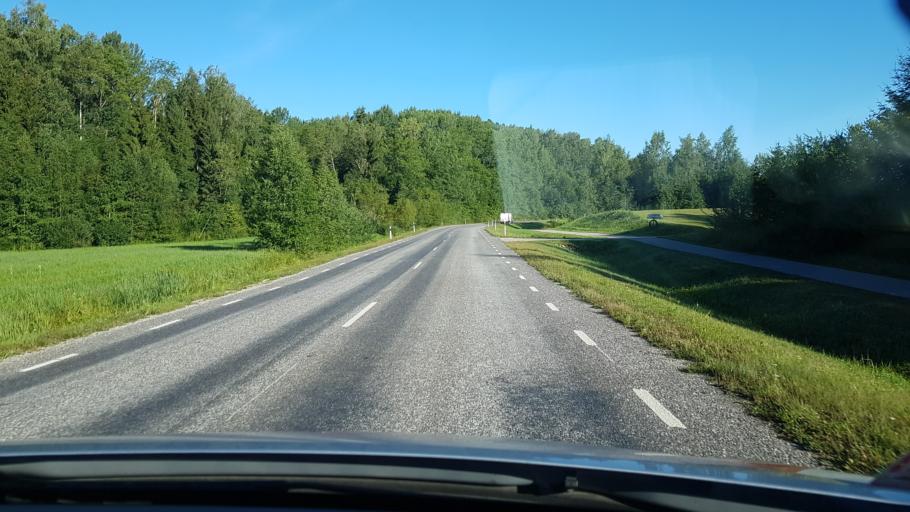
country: EE
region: Vorumaa
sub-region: Antsla vald
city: Vana-Antsla
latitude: 58.0442
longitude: 26.5480
